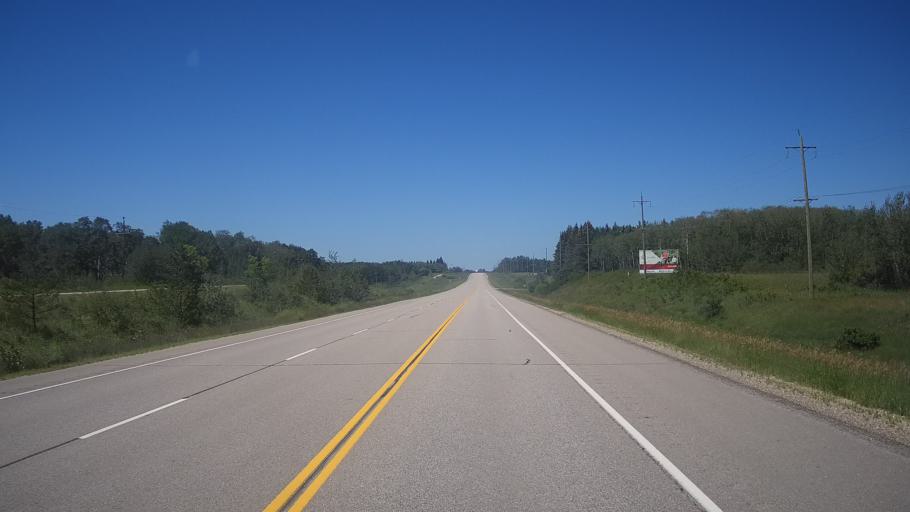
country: CA
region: Manitoba
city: Neepawa
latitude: 50.2254
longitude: -99.3541
